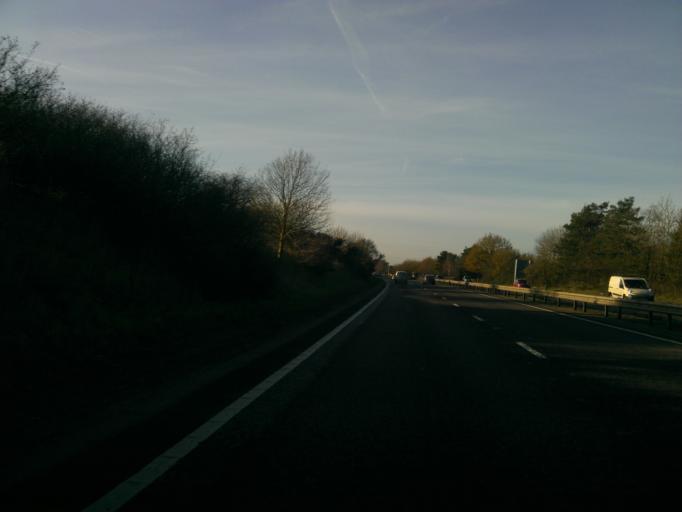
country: GB
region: England
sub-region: Essex
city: Great Horkesley
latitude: 51.9227
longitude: 0.8887
